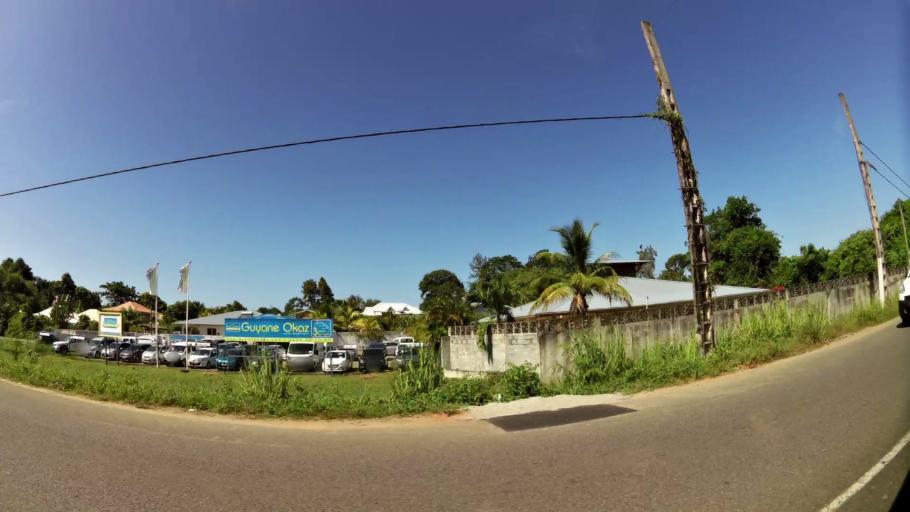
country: GF
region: Guyane
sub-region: Guyane
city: Remire-Montjoly
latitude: 4.9175
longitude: -52.2770
